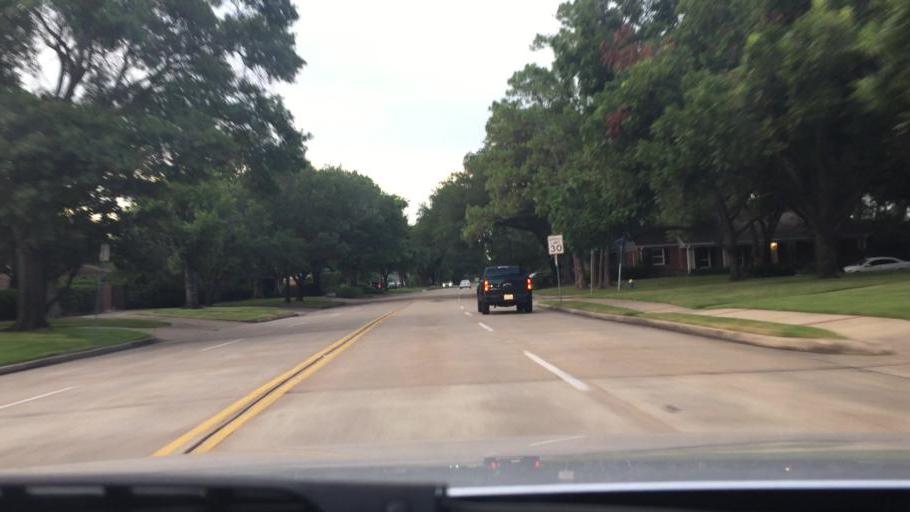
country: US
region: Texas
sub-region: Harris County
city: Hunters Creek Village
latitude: 29.7455
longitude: -95.4773
